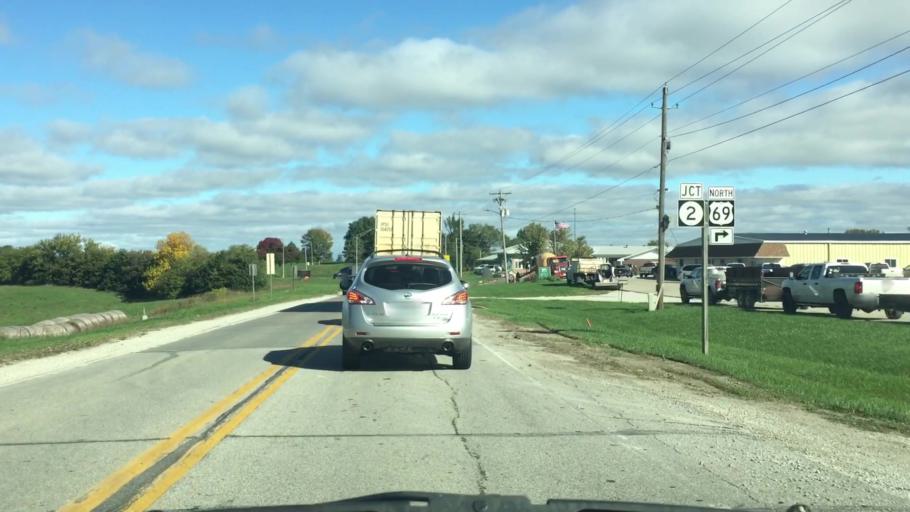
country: US
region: Iowa
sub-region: Decatur County
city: Leon
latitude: 40.7372
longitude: -93.7611
